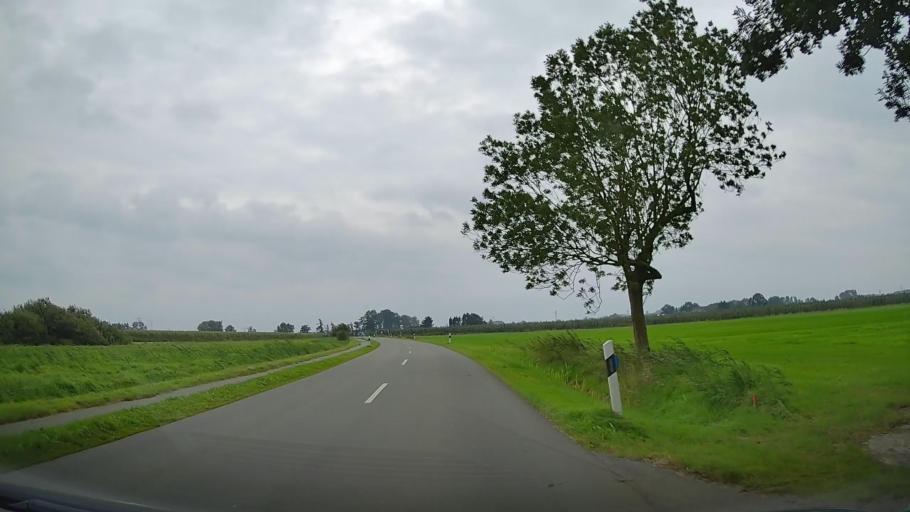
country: DE
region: Lower Saxony
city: Stade
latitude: 53.6328
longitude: 9.4640
